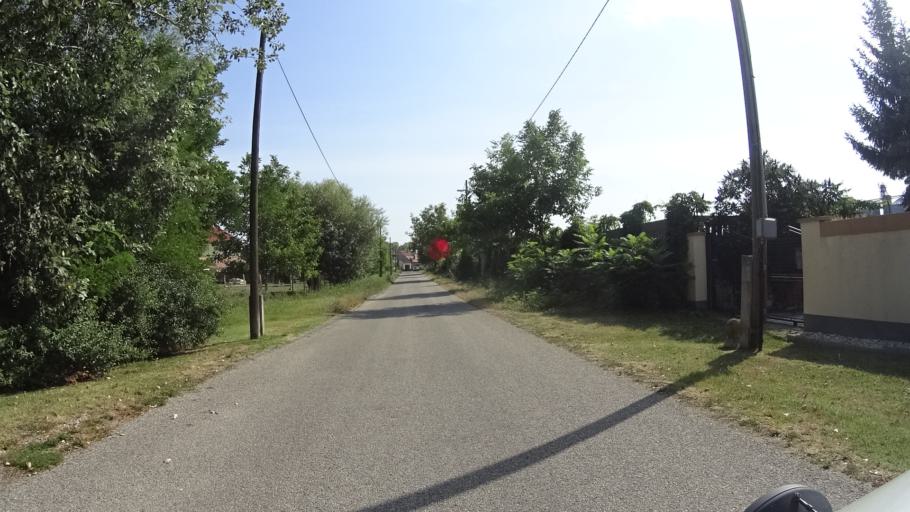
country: HU
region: Gyor-Moson-Sopron
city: Gyor
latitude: 47.6800
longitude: 17.6060
